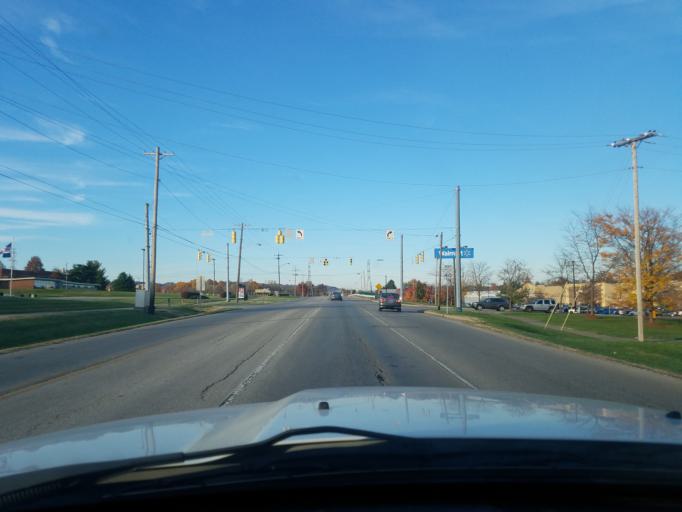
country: US
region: Indiana
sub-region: Floyd County
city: New Albany
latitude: 38.3176
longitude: -85.8205
